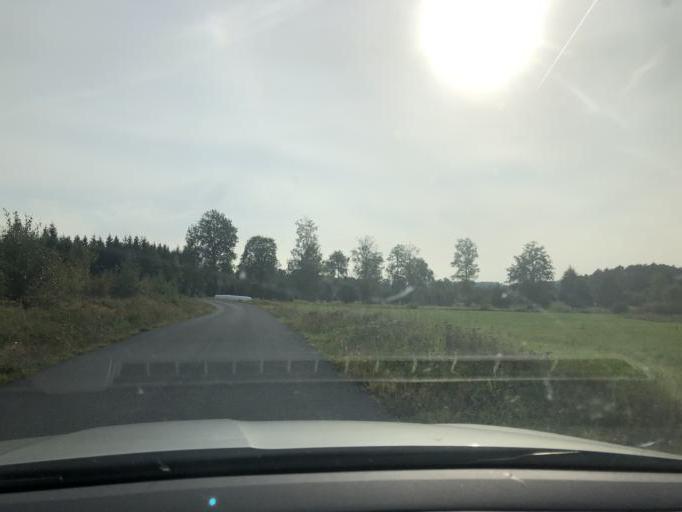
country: SE
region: Joenkoeping
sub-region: Vetlanda Kommun
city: Ekenassjon
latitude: 57.4905
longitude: 14.8934
